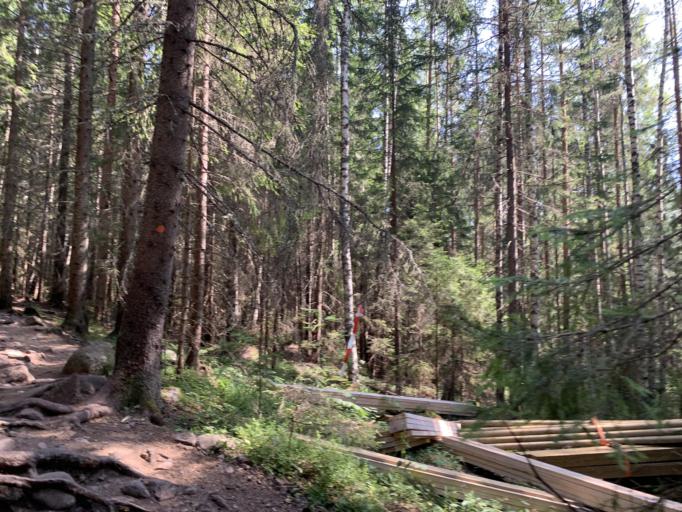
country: SE
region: Vaesternorrland
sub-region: OErnskoeldsviks Kommun
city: Kopmanholmen
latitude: 63.0882
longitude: 18.4931
